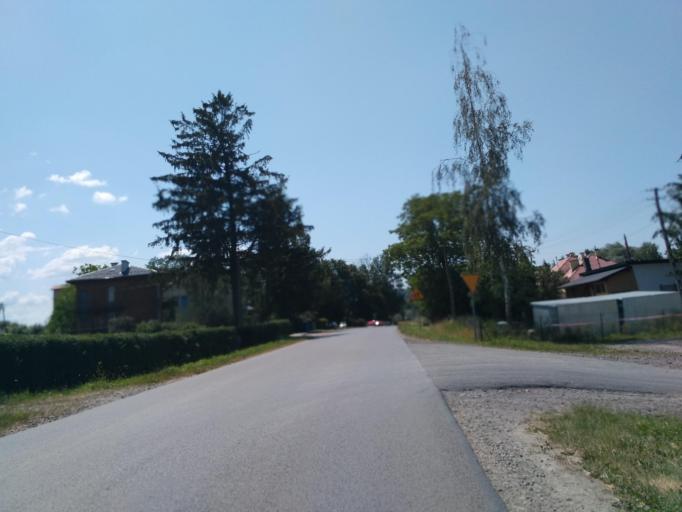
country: PL
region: Subcarpathian Voivodeship
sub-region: Powiat sanocki
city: Niebieszczany
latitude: 49.5286
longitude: 22.1279
